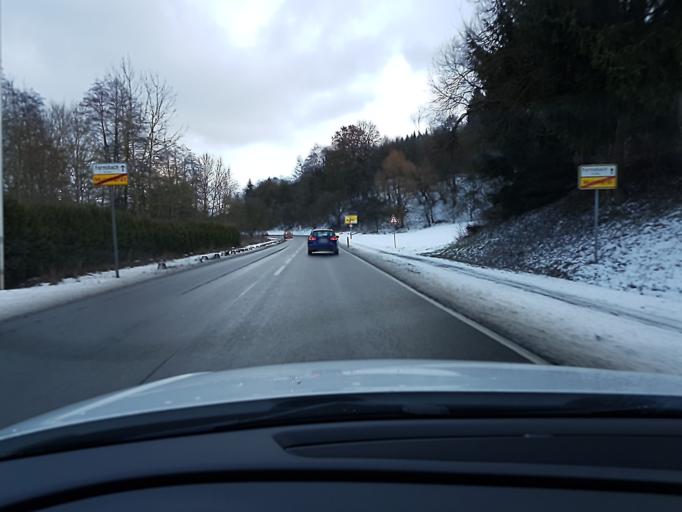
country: DE
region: Baden-Wuerttemberg
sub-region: Regierungsbezirk Stuttgart
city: Murrhardt
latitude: 48.9754
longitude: 9.5995
